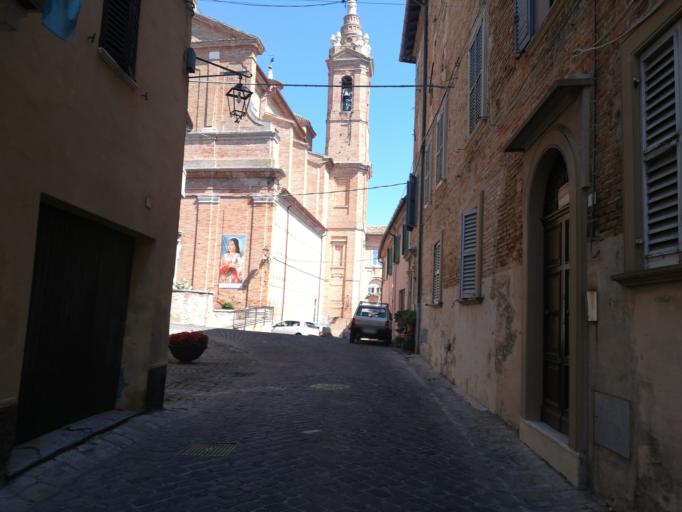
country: IT
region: The Marches
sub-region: Provincia di Ancona
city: Corinaldo
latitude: 43.6494
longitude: 13.0467
